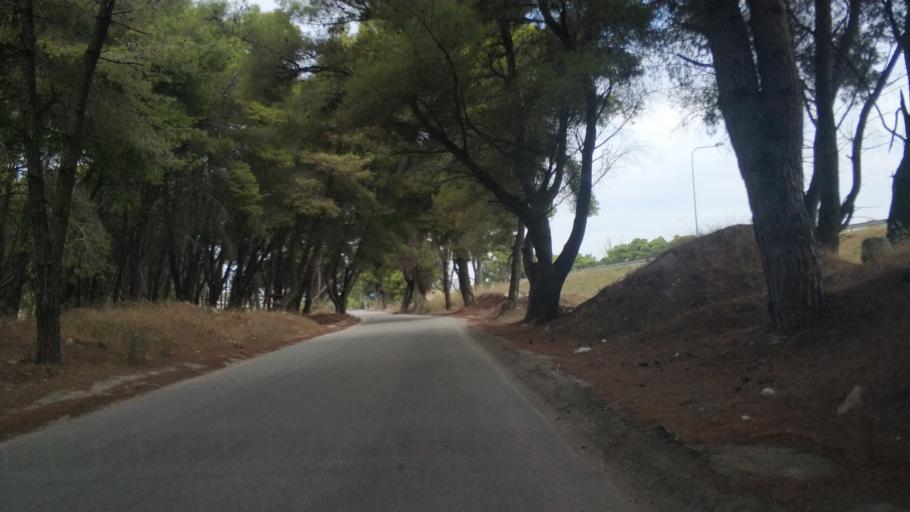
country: AL
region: Vlore
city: Vlore
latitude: 40.4697
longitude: 19.4598
